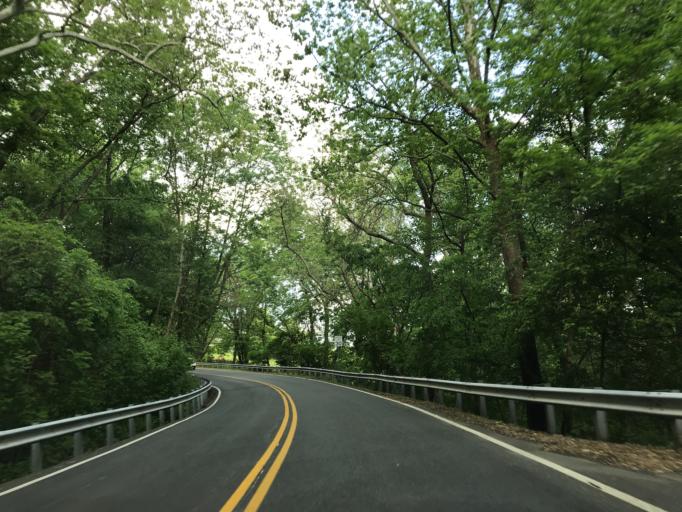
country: US
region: Maryland
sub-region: Harford County
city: Bel Air North
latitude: 39.5299
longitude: -76.3836
